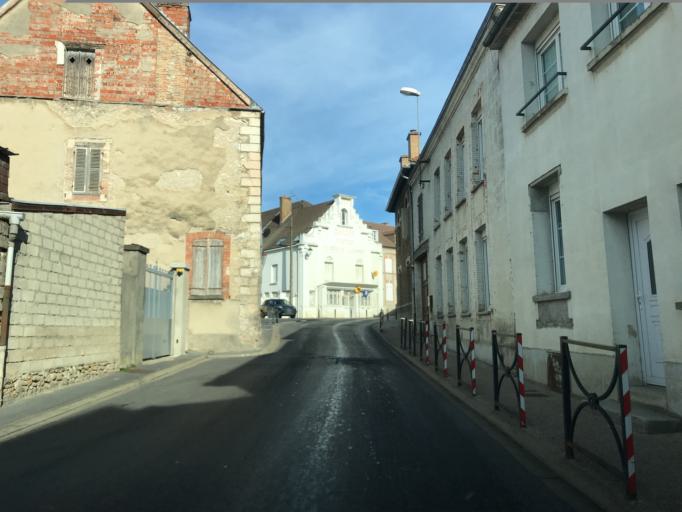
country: FR
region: Champagne-Ardenne
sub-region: Departement de la Marne
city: Damery
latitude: 49.0714
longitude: 3.8784
